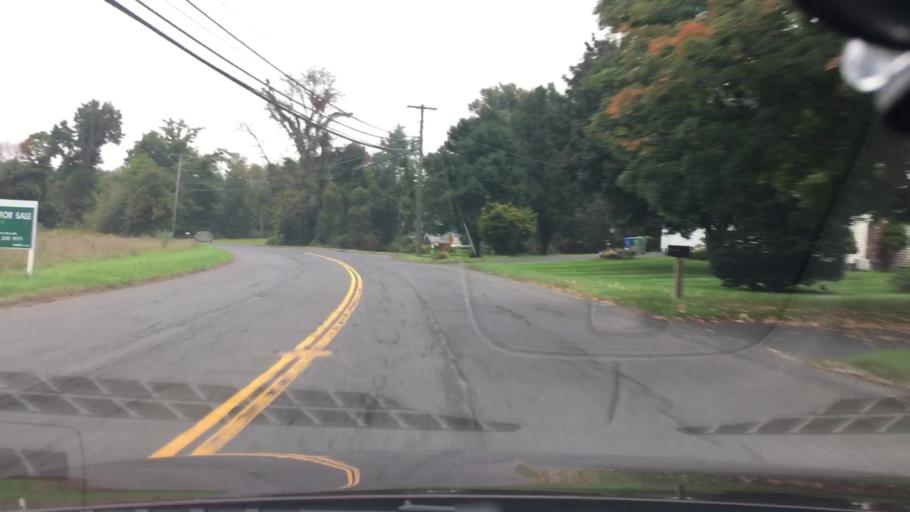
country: US
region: Connecticut
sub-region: Middlesex County
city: Middletown
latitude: 41.5739
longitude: -72.7238
